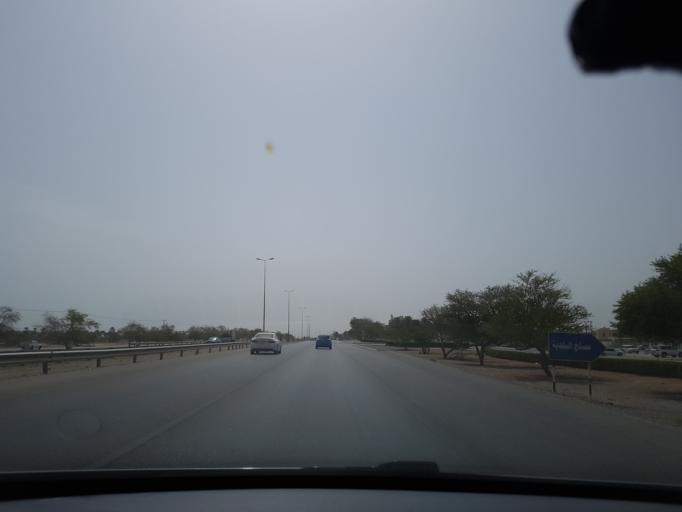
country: OM
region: Al Batinah
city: As Suwayq
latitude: 23.8302
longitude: 57.4037
